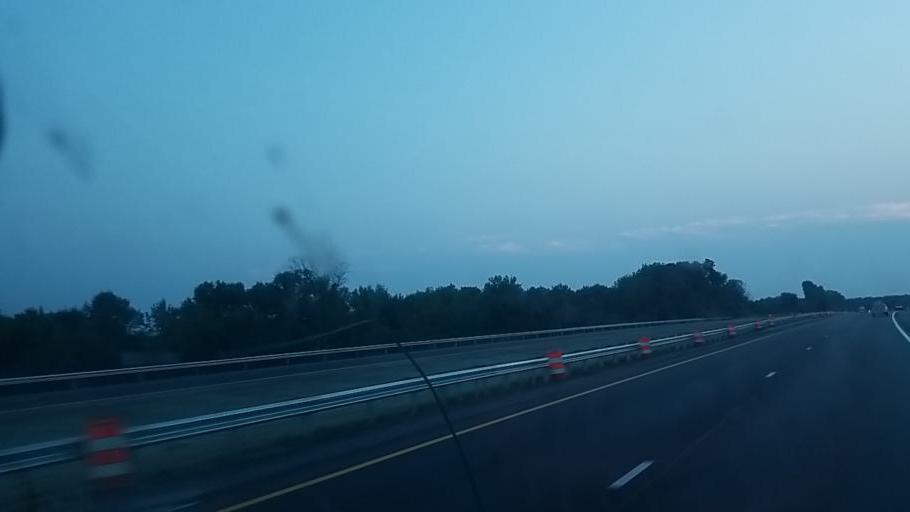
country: US
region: New York
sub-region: Oneida County
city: Clark Mills
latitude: 43.1237
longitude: -75.3807
